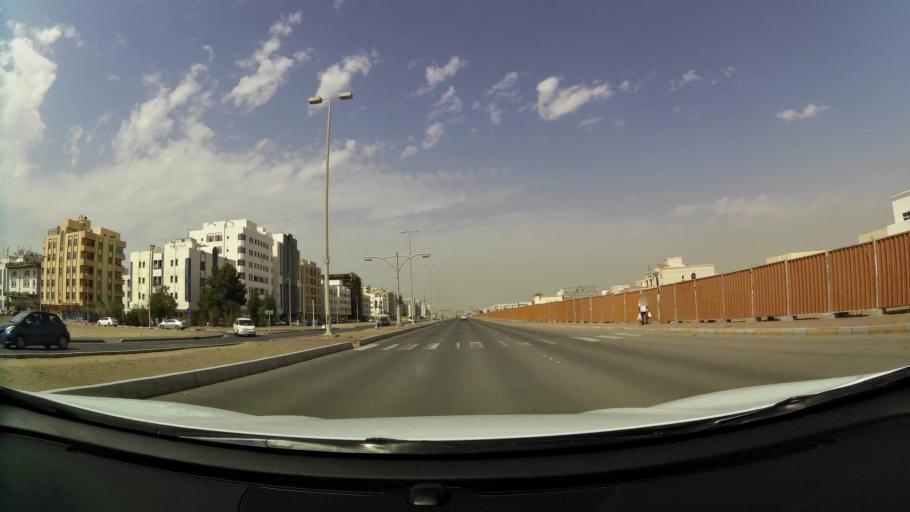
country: AE
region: Abu Dhabi
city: Abu Dhabi
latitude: 24.3334
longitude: 54.5388
